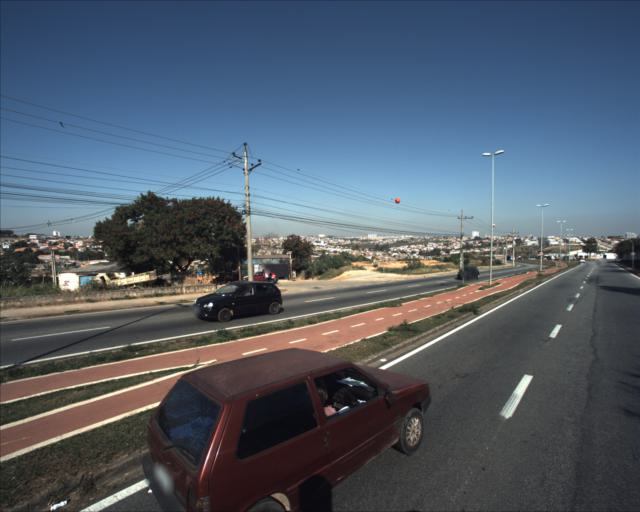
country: BR
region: Sao Paulo
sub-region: Sorocaba
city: Sorocaba
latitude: -23.4850
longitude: -47.4866
